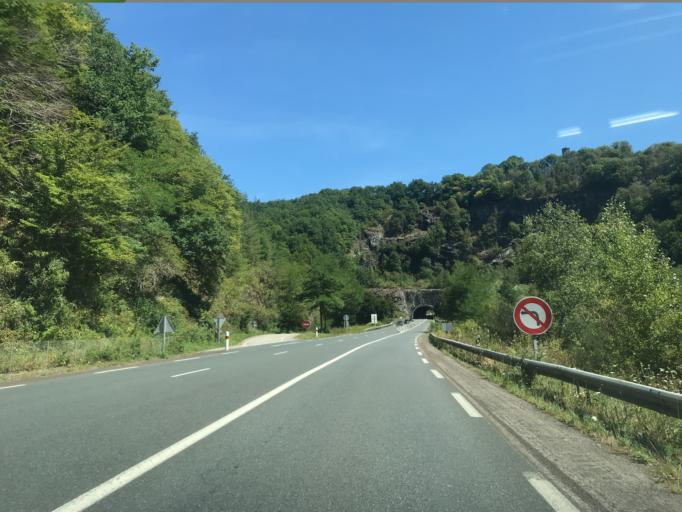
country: FR
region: Limousin
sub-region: Departement de la Correze
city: Cornil
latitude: 45.2118
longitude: 1.6855
